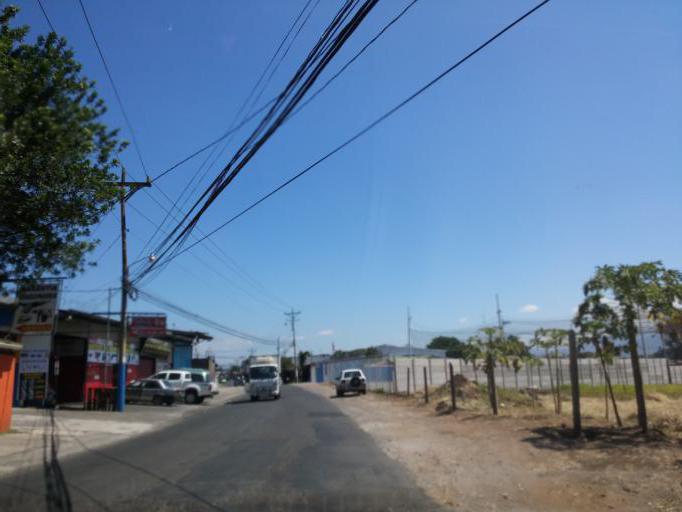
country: CR
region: Alajuela
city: Alajuela
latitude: 10.0045
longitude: -84.2254
